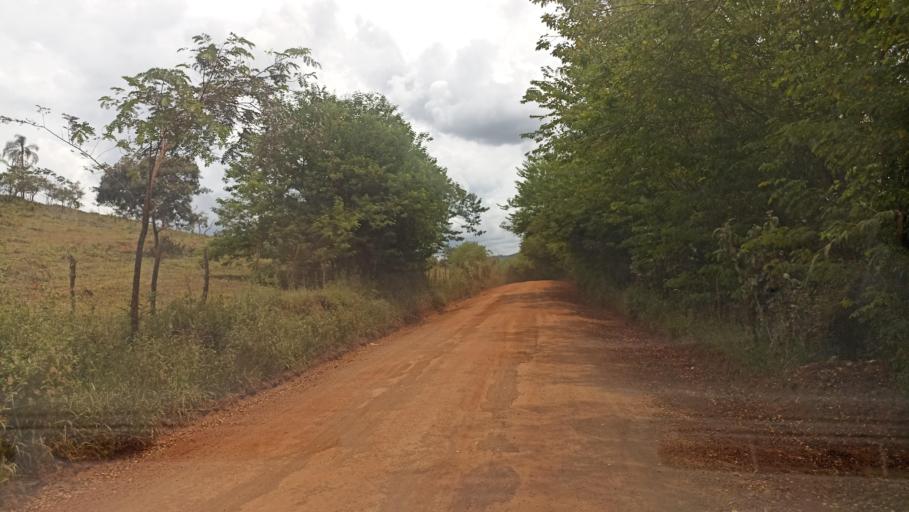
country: BR
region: Minas Gerais
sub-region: Itabirito
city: Itabirito
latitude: -20.3474
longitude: -43.7429
